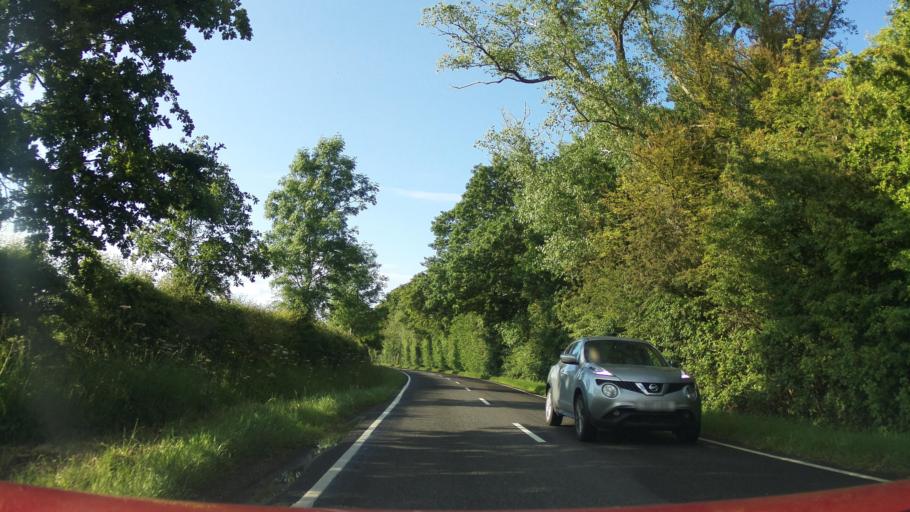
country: GB
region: England
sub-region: Lincolnshire
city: Great Gonerby
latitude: 53.0571
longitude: -0.6413
